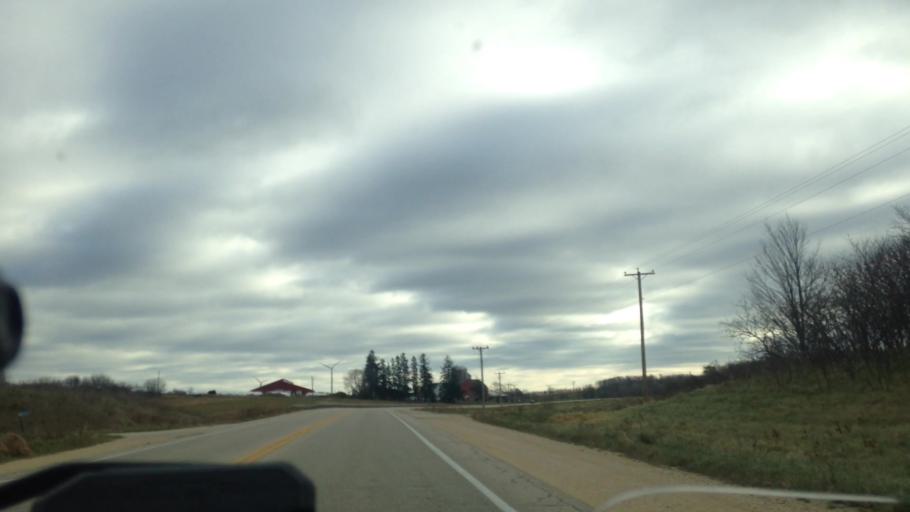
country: US
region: Wisconsin
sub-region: Dodge County
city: Mayville
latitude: 43.4430
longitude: -88.4959
